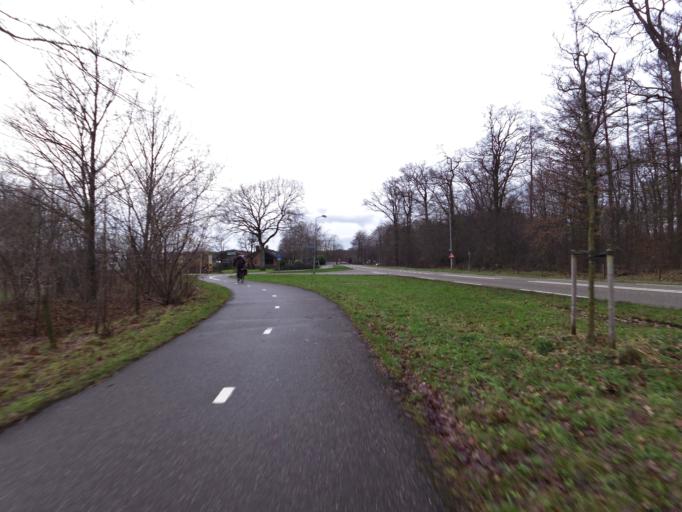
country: NL
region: Gelderland
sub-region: Oude IJsselstreek
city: Wisch
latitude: 51.9542
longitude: 6.3780
